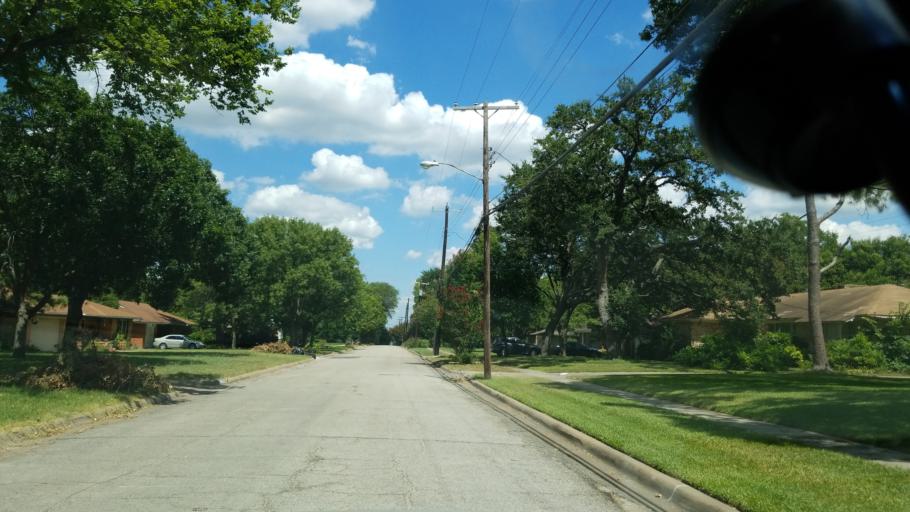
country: US
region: Texas
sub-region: Dallas County
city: Cockrell Hill
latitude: 32.7000
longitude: -96.8669
